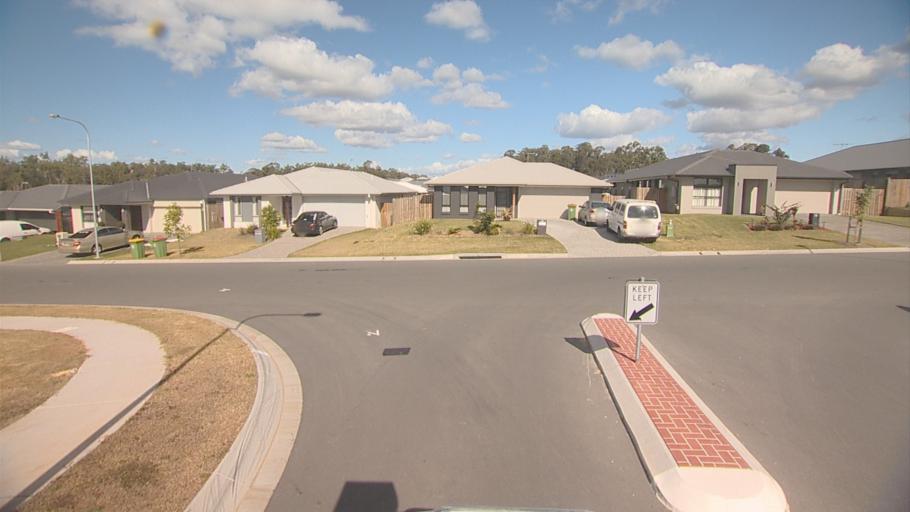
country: AU
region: Queensland
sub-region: Logan
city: Logan Reserve
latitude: -27.7140
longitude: 153.0854
